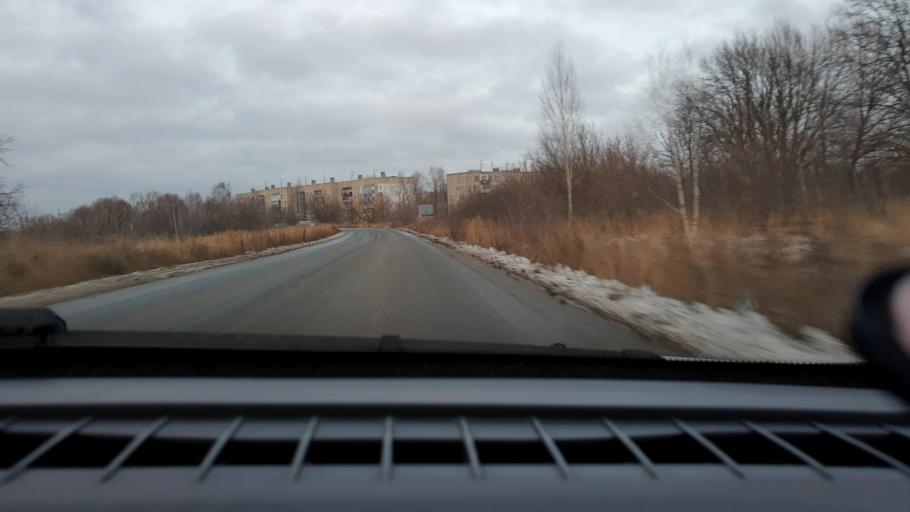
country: RU
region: Nizjnij Novgorod
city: Gorbatovka
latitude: 56.2418
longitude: 43.7447
